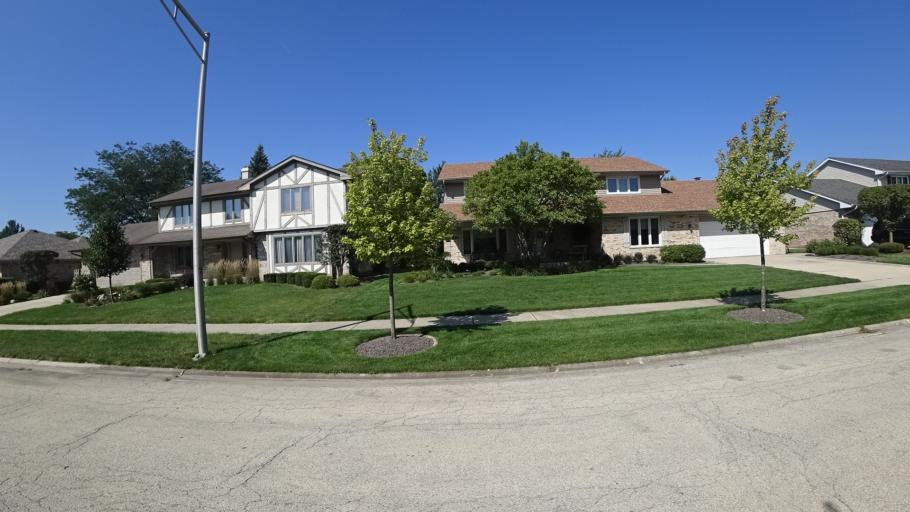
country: US
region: Illinois
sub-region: Cook County
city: Palos Park
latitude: 41.6347
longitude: -87.8168
